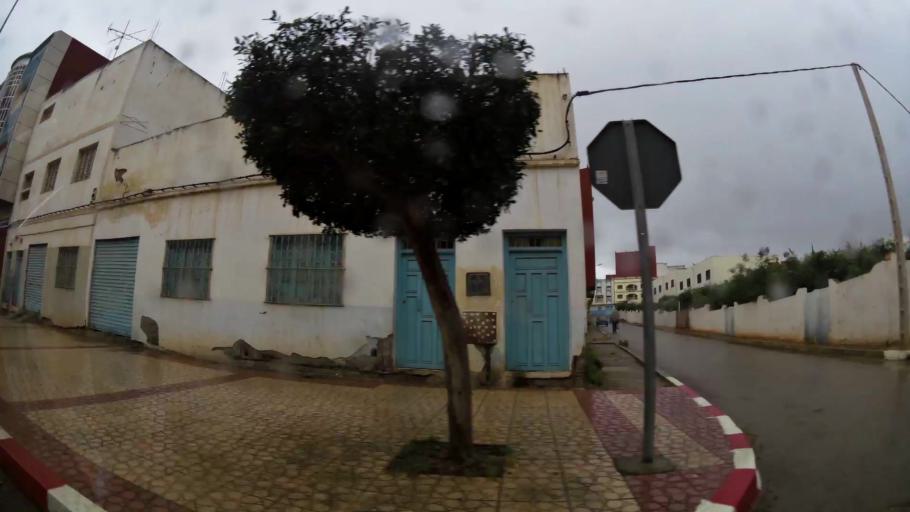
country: MA
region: Taza-Al Hoceima-Taounate
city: Imzourene
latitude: 35.1387
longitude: -3.8525
